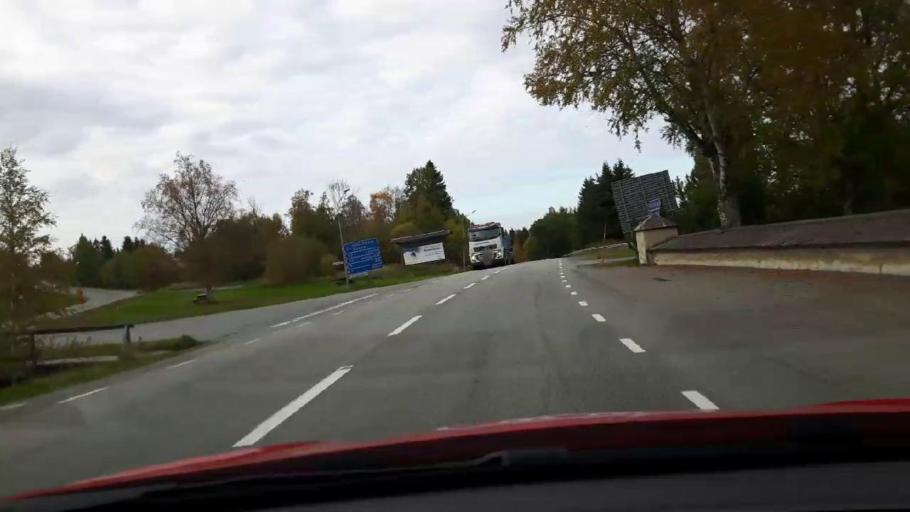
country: SE
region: Jaemtland
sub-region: Krokoms Kommun
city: Krokom
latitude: 63.1783
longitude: 14.0897
